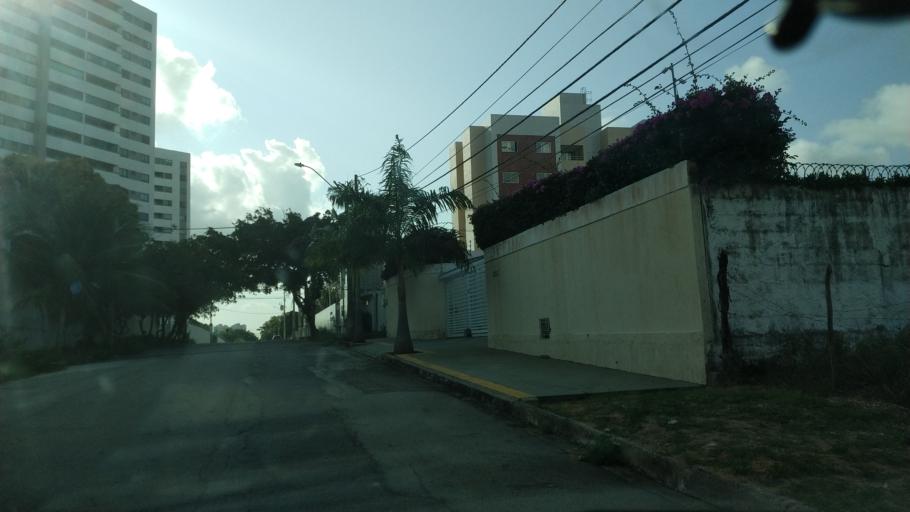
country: BR
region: Rio Grande do Norte
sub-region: Natal
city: Natal
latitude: -5.8633
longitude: -35.1987
